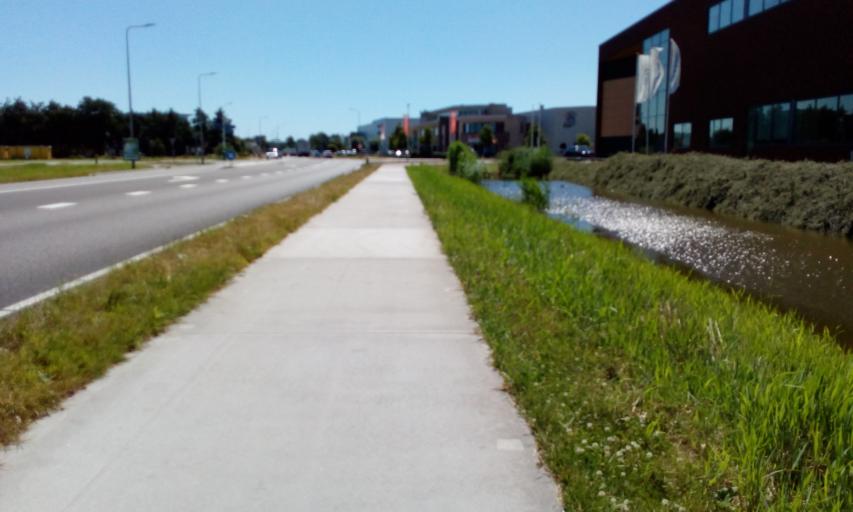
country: NL
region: South Holland
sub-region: Gemeente Teylingen
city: Voorhout
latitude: 52.2133
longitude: 4.4941
